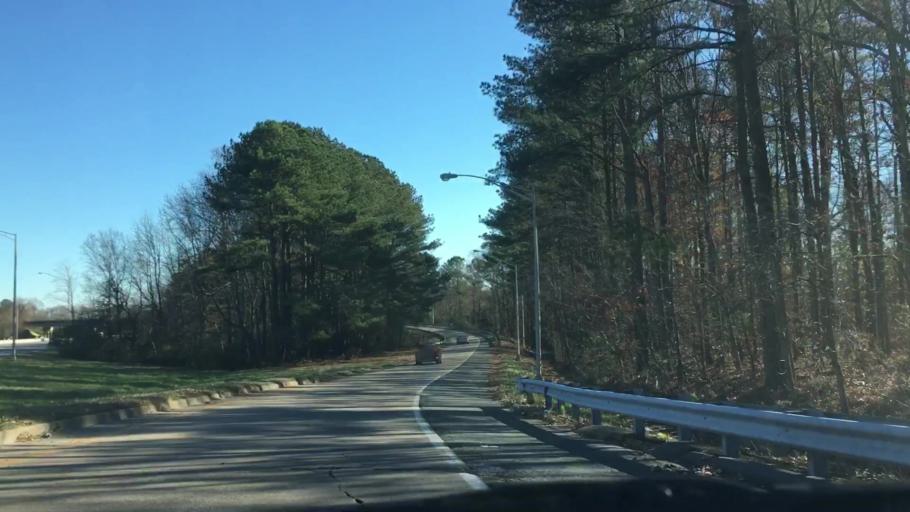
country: US
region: Virginia
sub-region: City of Virginia Beach
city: Virginia Beach
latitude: 36.8414
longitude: -76.0458
